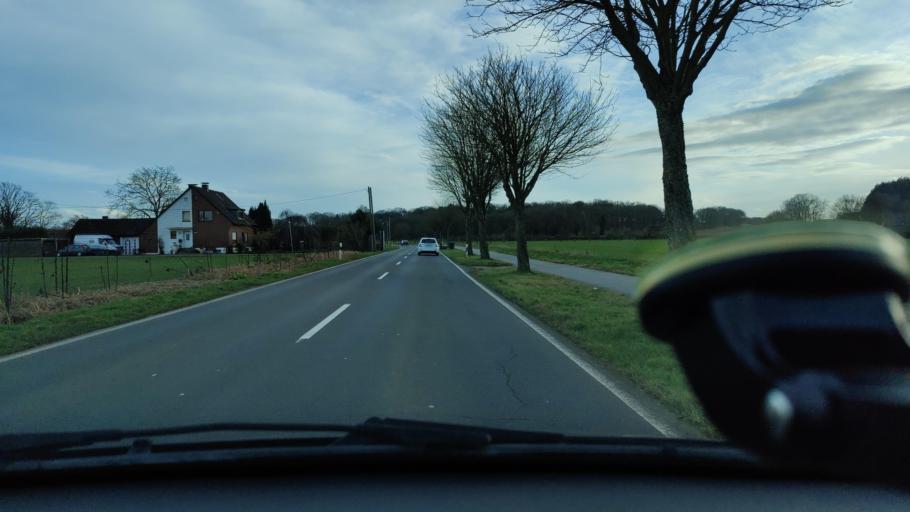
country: DE
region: North Rhine-Westphalia
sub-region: Regierungsbezirk Dusseldorf
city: Alpen
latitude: 51.5930
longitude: 6.4657
